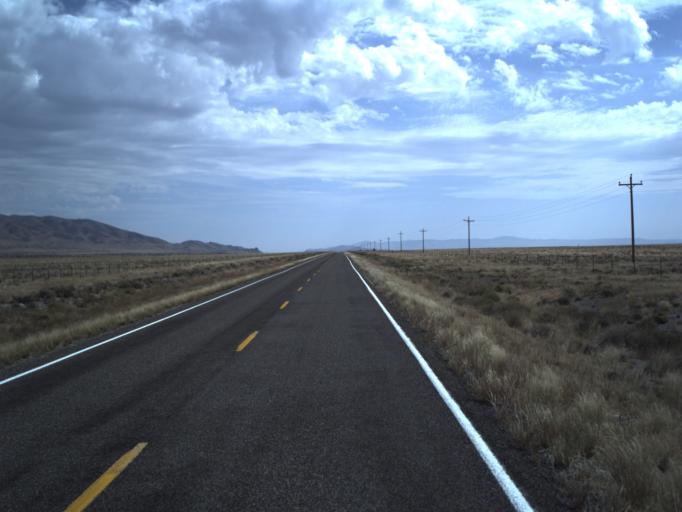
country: US
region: Utah
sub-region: Tooele County
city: Wendover
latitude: 41.4304
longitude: -113.8046
